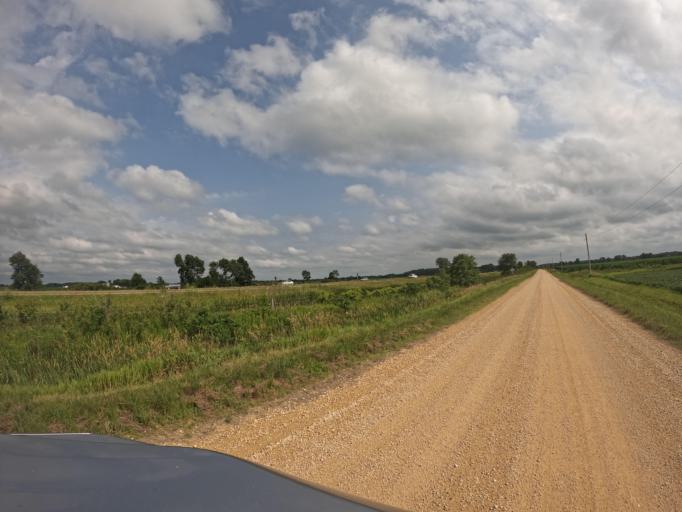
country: US
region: Iowa
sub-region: Clinton County
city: De Witt
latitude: 41.7828
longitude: -90.5684
